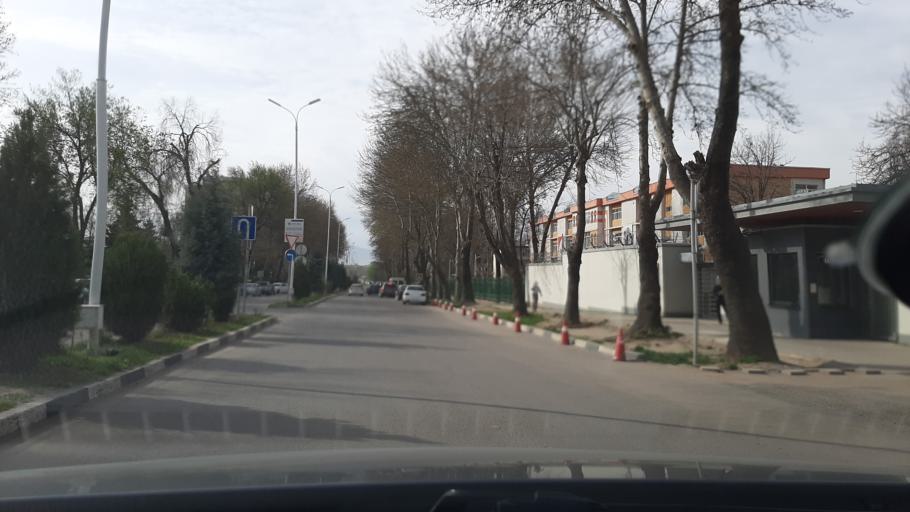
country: TJ
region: Dushanbe
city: Dushanbe
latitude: 38.5811
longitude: 68.7490
